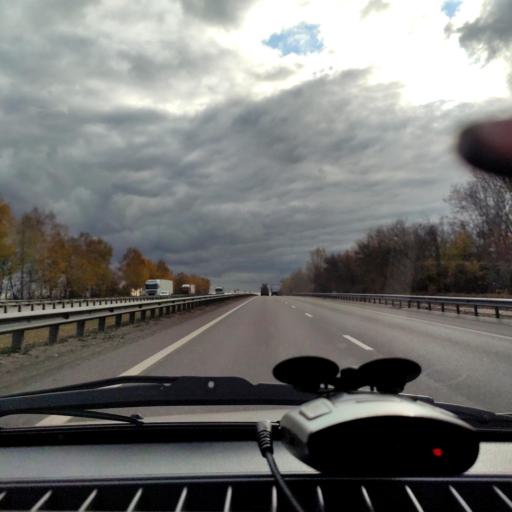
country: RU
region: Voronezj
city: Ramon'
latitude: 51.9165
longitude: 39.2197
